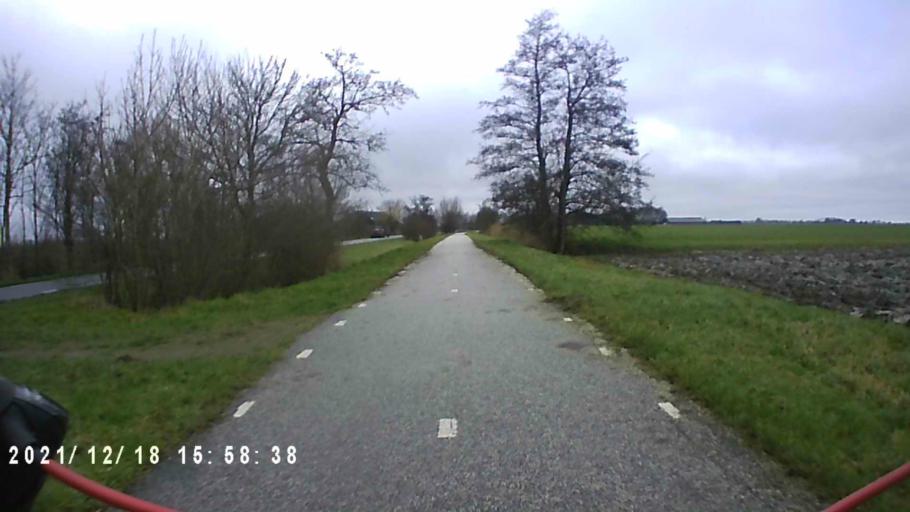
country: NL
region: Friesland
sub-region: Gemeente Dongeradeel
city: Anjum
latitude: 53.3374
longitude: 6.0922
